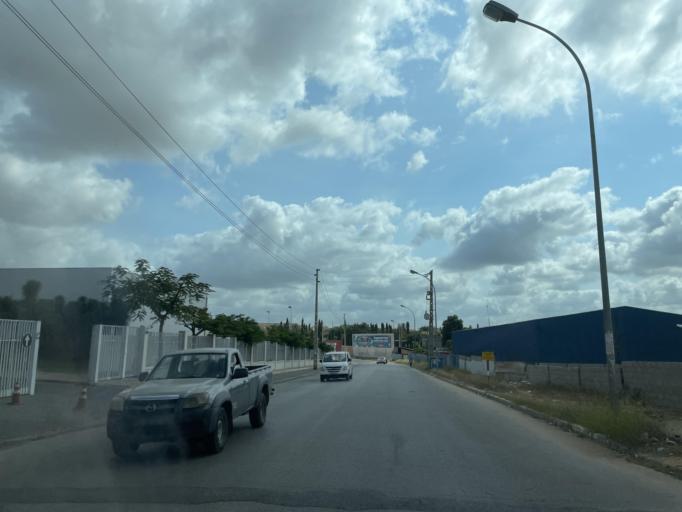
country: AO
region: Luanda
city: Luanda
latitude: -8.9204
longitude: 13.2035
